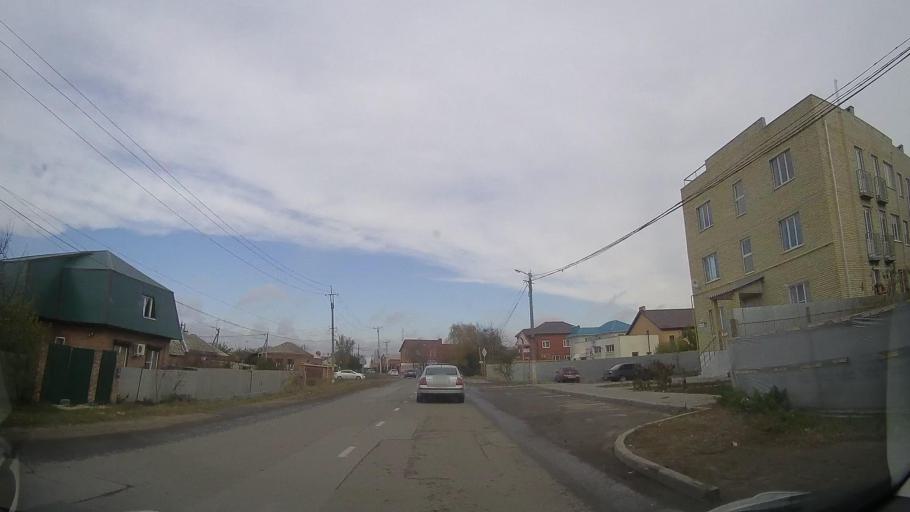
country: RU
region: Rostov
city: Bataysk
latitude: 47.1502
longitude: 39.7668
